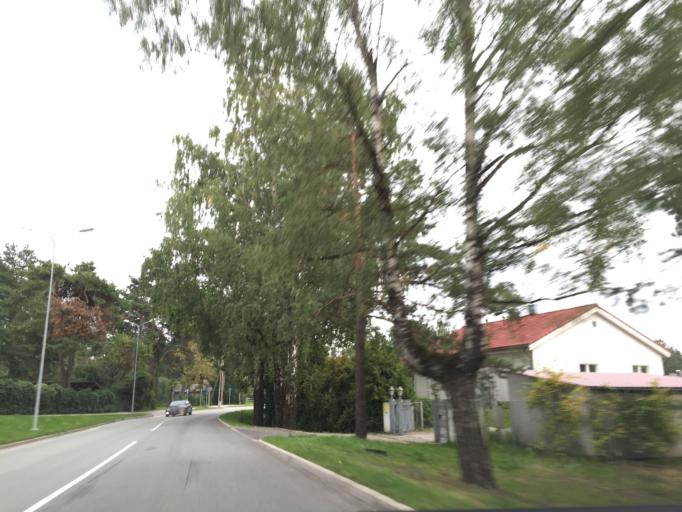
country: LV
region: Ogre
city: Ogre
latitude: 56.8146
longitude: 24.6300
